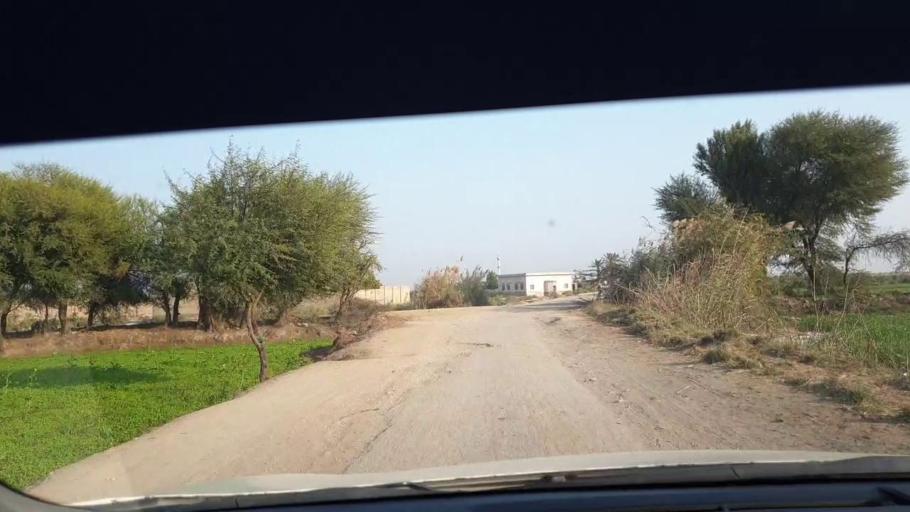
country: PK
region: Sindh
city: Berani
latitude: 25.8413
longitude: 68.7789
